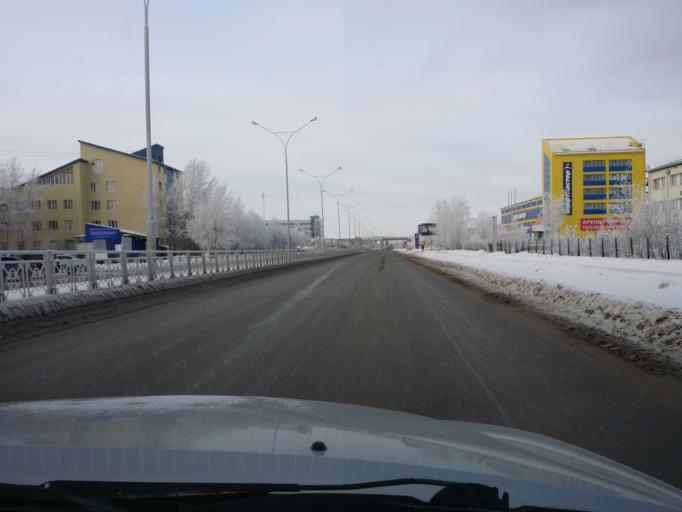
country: RU
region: Khanty-Mansiyskiy Avtonomnyy Okrug
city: Nizhnevartovsk
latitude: 60.9392
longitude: 76.5404
